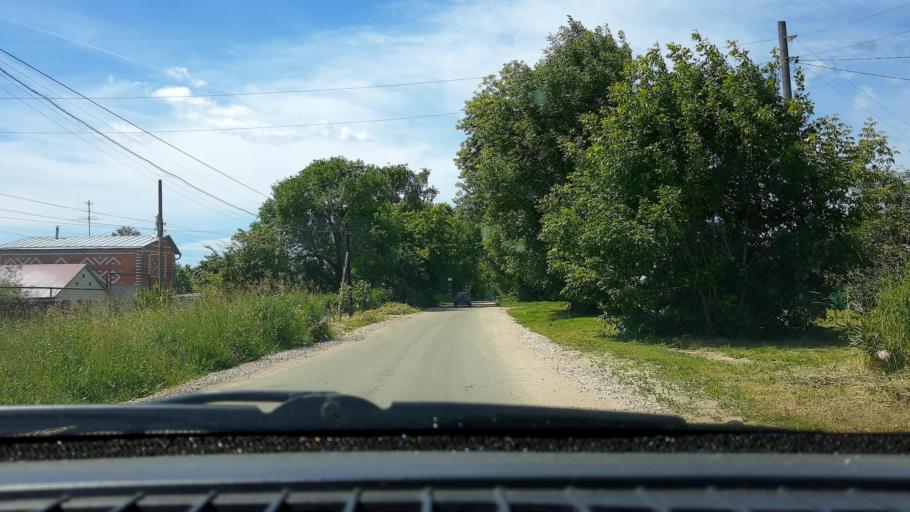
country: RU
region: Nizjnij Novgorod
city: Burevestnik
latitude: 56.1886
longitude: 43.9338
